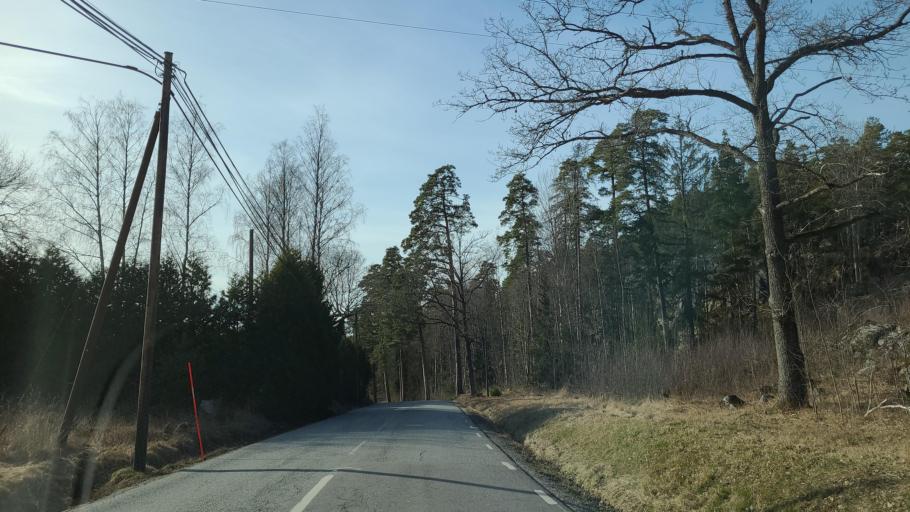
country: SE
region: Stockholm
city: Stenhamra
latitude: 59.2771
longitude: 17.6835
